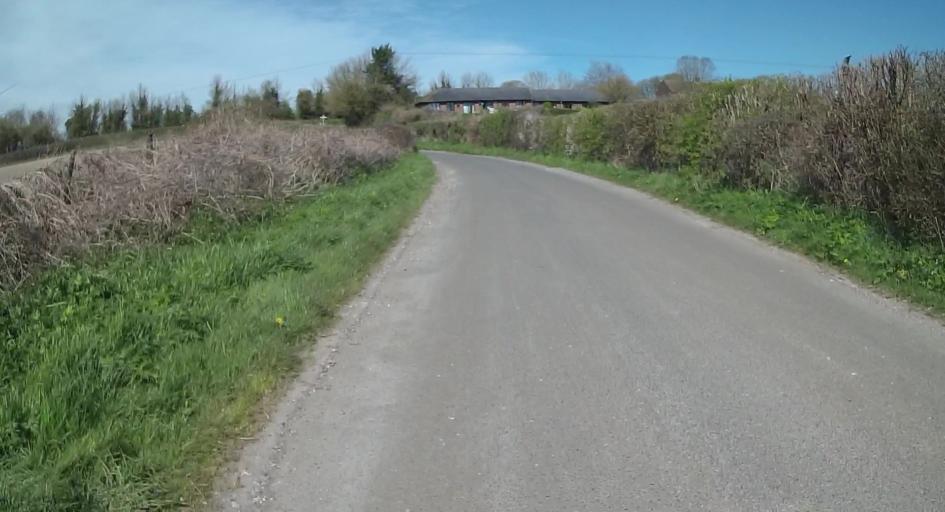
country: GB
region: England
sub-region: Hampshire
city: Hook
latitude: 51.2521
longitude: -0.9768
